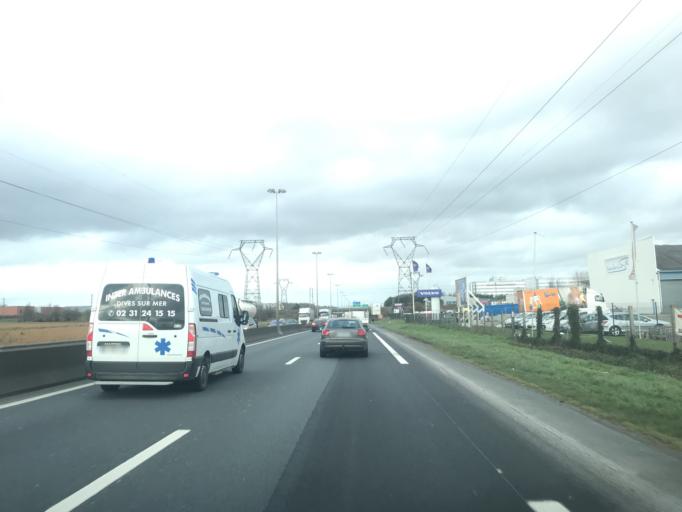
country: FR
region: Lower Normandy
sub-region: Departement du Calvados
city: Mondeville
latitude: 49.1590
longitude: -0.3103
